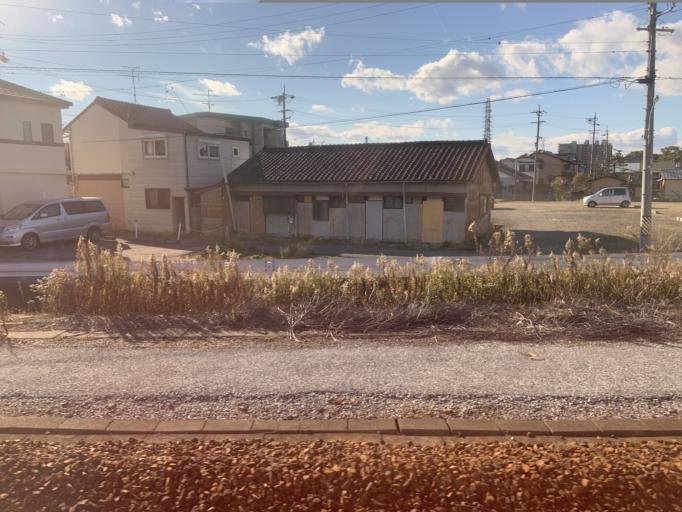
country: JP
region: Aichi
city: Inazawa
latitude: 35.2557
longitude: 136.8197
